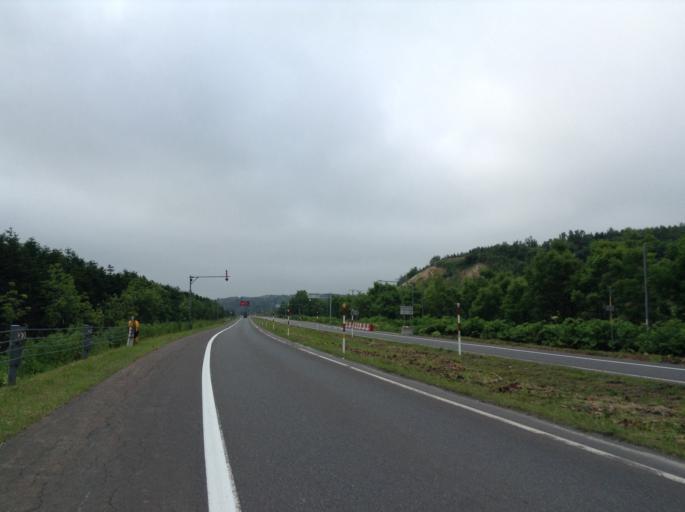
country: JP
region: Hokkaido
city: Wakkanai
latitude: 45.3678
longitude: 141.7277
